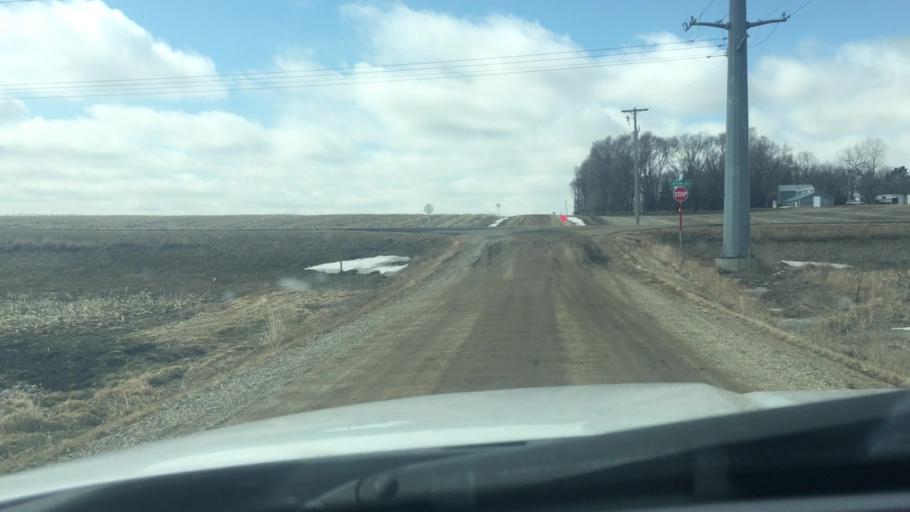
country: US
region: South Dakota
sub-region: Minnehaha County
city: Crooks
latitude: 43.6163
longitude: -96.8103
